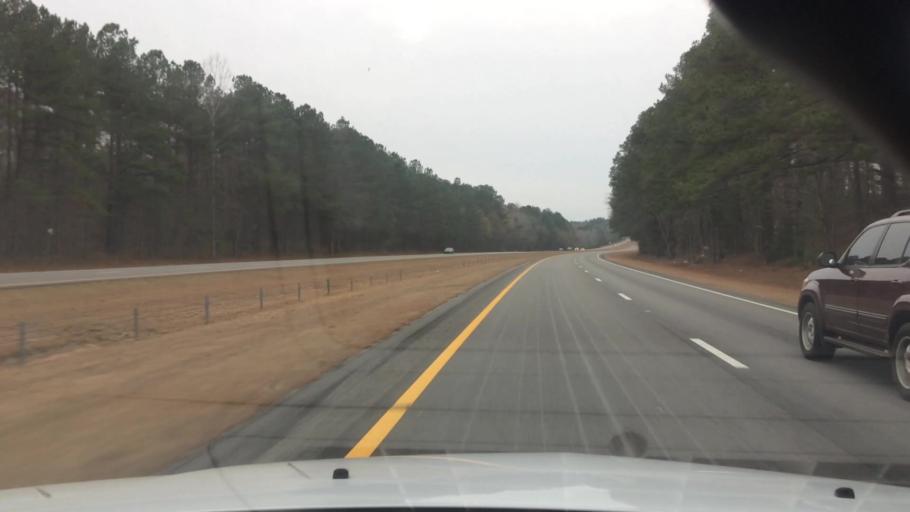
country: US
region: North Carolina
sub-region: Nash County
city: Spring Hope
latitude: 35.8920
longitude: -78.1954
